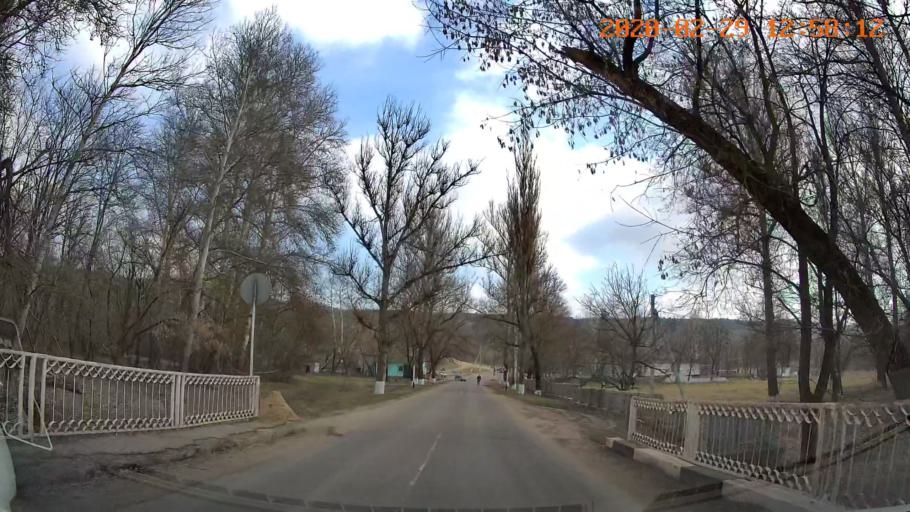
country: MD
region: Telenesti
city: Camenca
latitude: 48.0709
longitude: 28.7185
